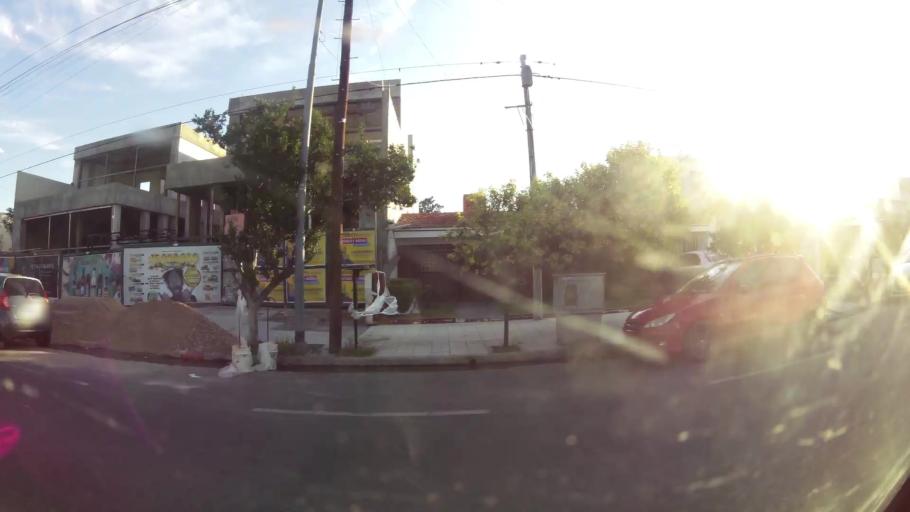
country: AR
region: Cordoba
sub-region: Departamento de Capital
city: Cordoba
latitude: -31.3833
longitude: -64.2363
